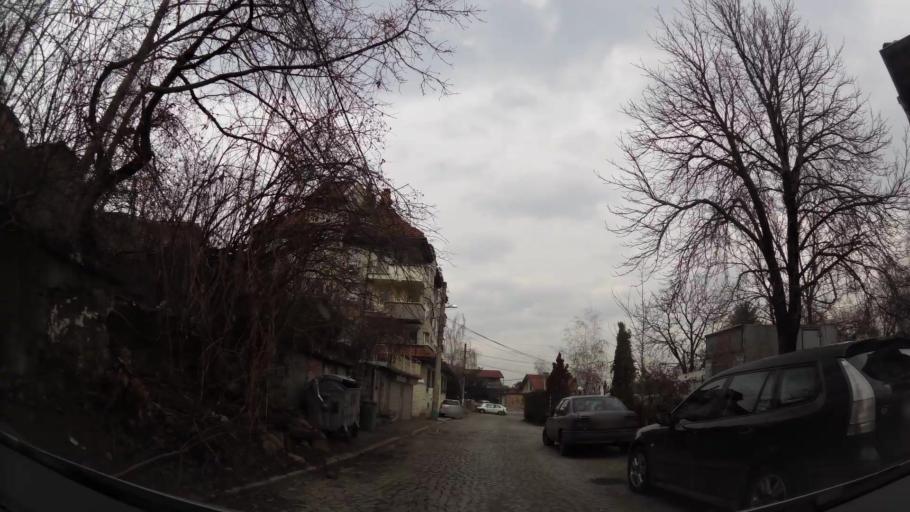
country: BG
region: Sofia-Capital
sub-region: Stolichna Obshtina
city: Sofia
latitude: 42.6637
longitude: 23.2431
